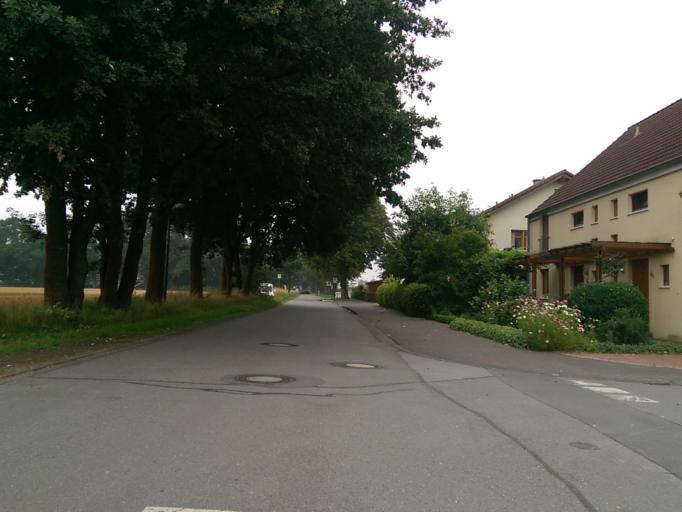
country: DE
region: North Rhine-Westphalia
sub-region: Regierungsbezirk Detmold
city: Guetersloh
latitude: 51.9085
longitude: 8.3450
